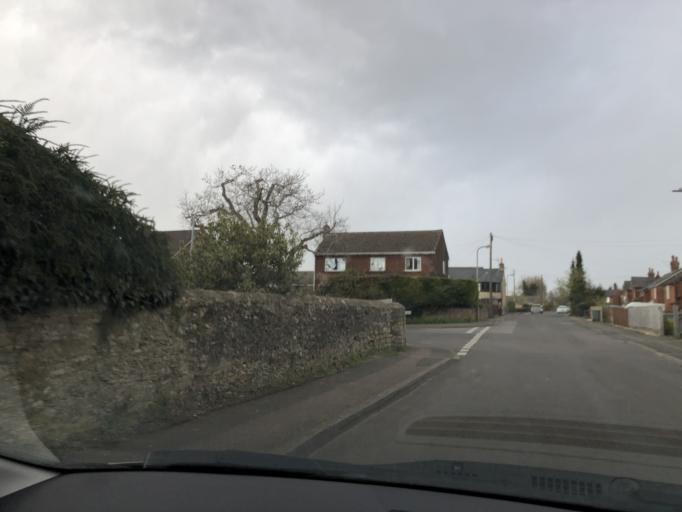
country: GB
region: England
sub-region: Oxfordshire
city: Bicester
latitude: 51.9055
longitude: -1.1643
